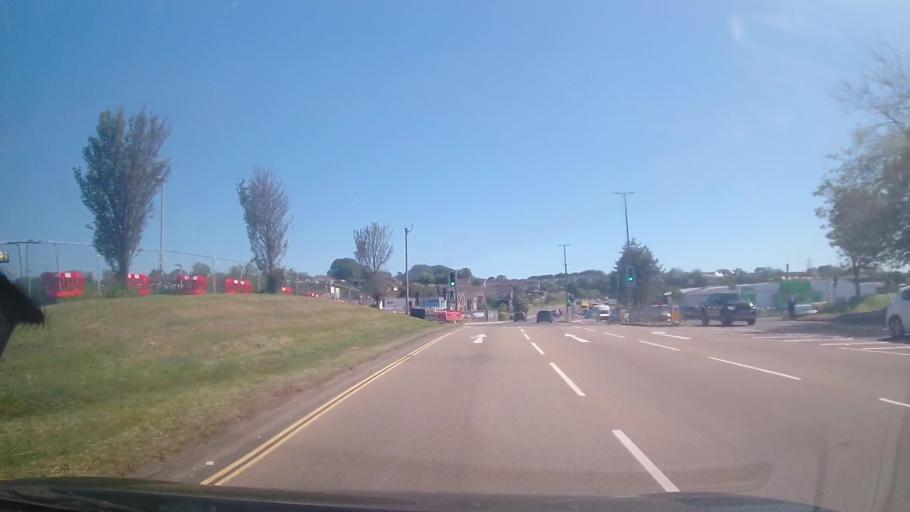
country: GB
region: England
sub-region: Borough of Torbay
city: Paignton
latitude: 50.4253
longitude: -3.5872
